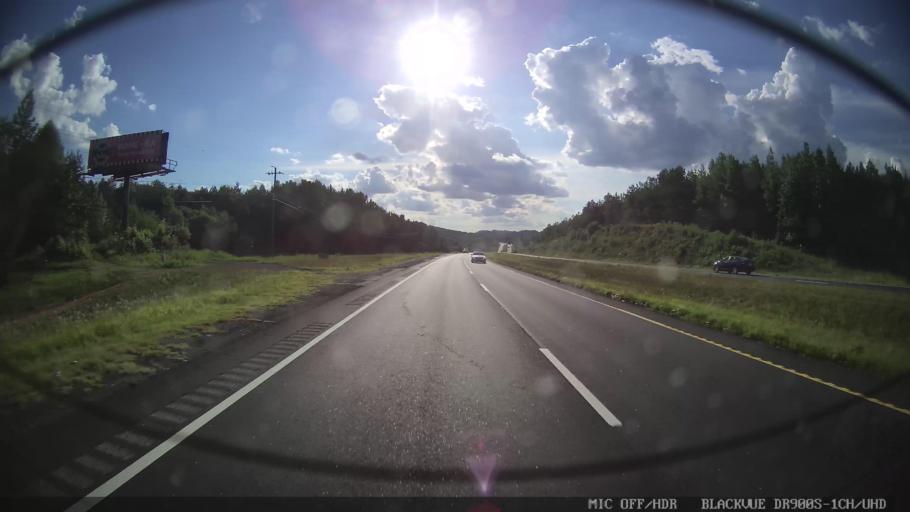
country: US
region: Georgia
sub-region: Floyd County
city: Rome
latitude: 34.2148
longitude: -85.1179
